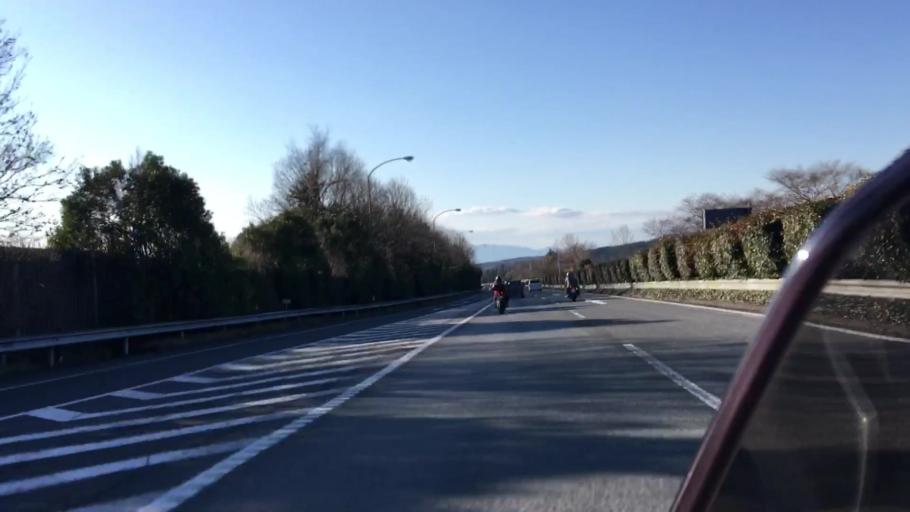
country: JP
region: Shizuoka
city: Gotemba
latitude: 35.2134
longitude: 138.9044
